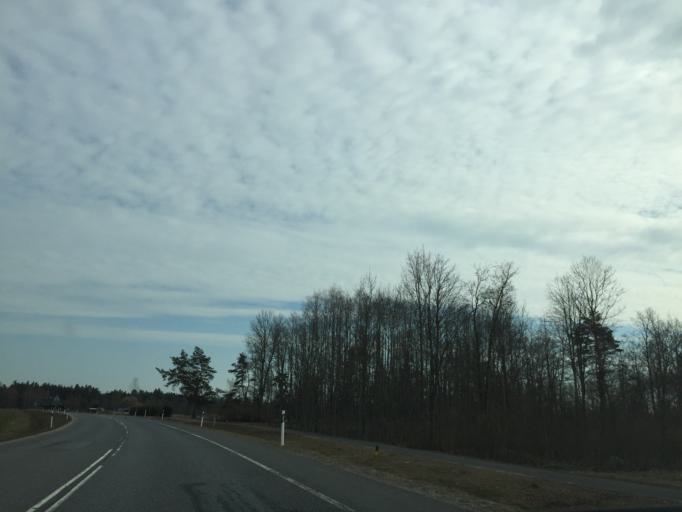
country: EE
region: Ida-Virumaa
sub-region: Johvi vald
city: Johvi
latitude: 59.2252
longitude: 27.5066
